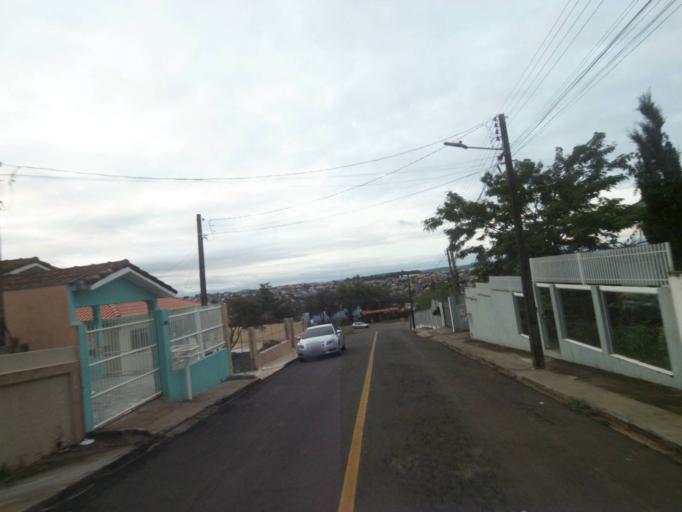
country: BR
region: Parana
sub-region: Telemaco Borba
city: Telemaco Borba
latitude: -24.3334
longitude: -50.6336
